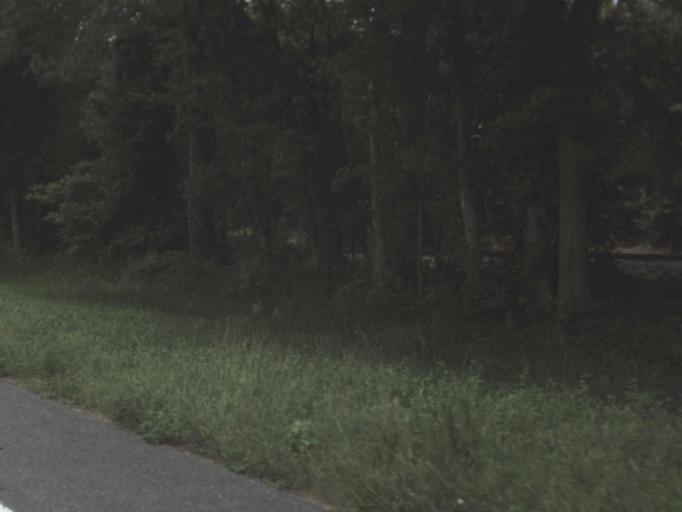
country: US
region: Florida
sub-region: Columbia County
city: Five Points
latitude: 30.3042
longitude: -82.7104
